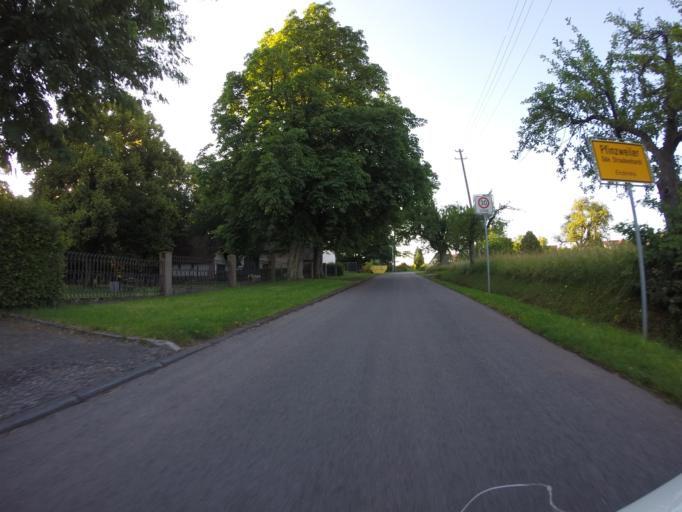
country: DE
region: Baden-Wuerttemberg
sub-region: Karlsruhe Region
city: Dobel
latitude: 48.8558
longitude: 8.5138
